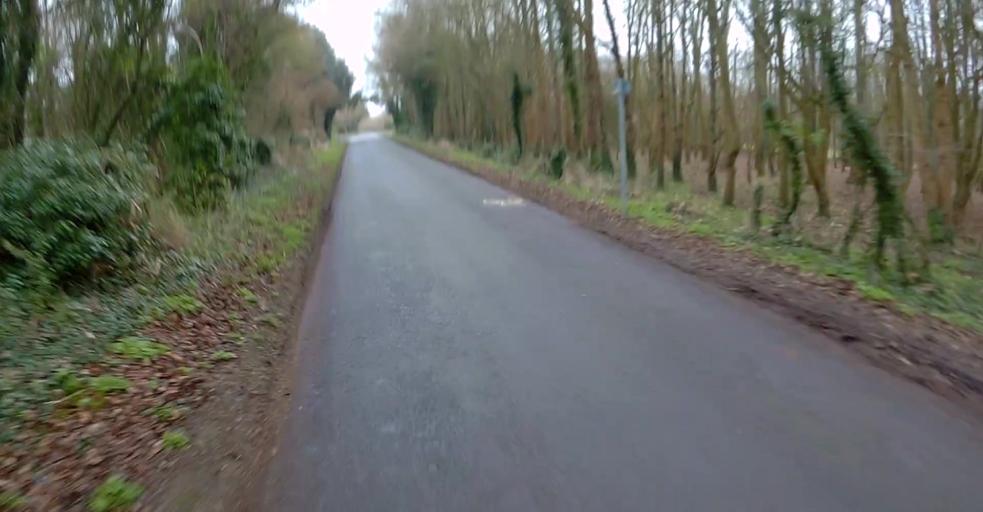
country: GB
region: England
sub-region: Hampshire
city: Old Basing
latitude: 51.2733
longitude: -1.0570
